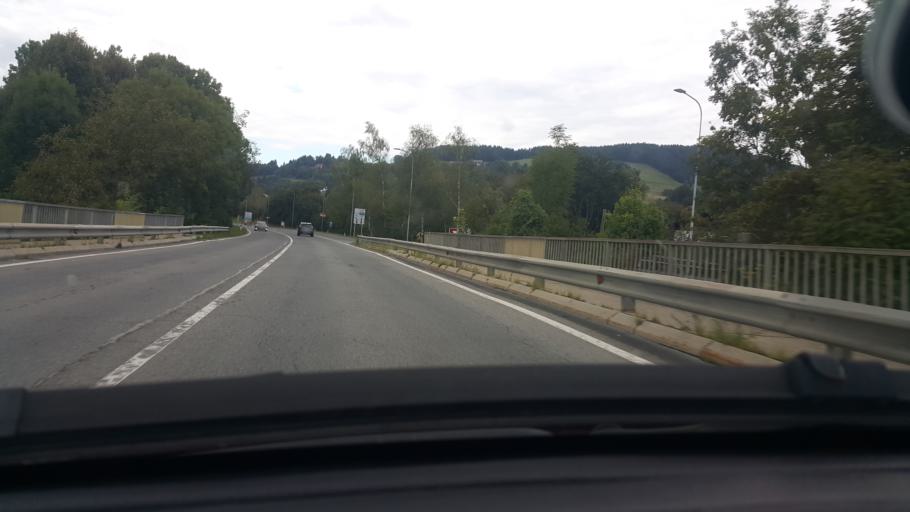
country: AT
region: Carinthia
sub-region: Politischer Bezirk Feldkirchen
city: Feldkirchen in Karnten
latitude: 46.7216
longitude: 14.1053
